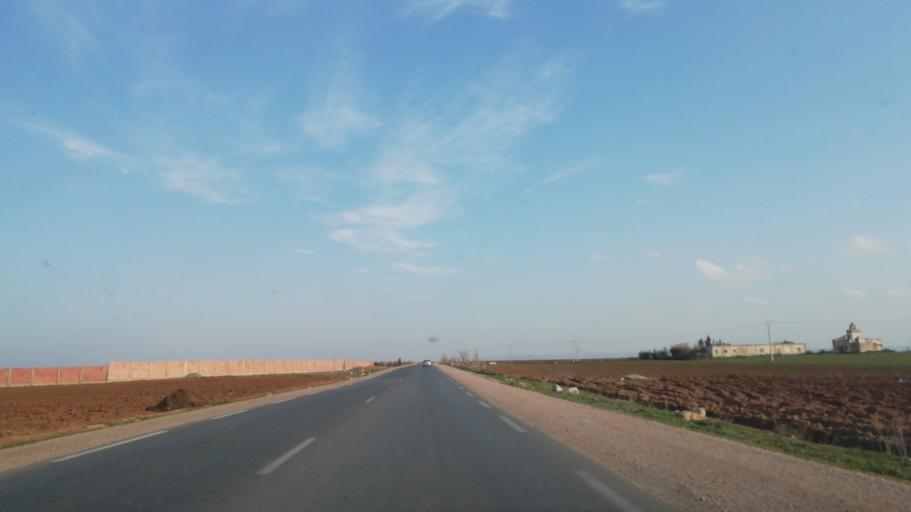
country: DZ
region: Relizane
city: Relizane
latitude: 35.8931
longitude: 0.6136
